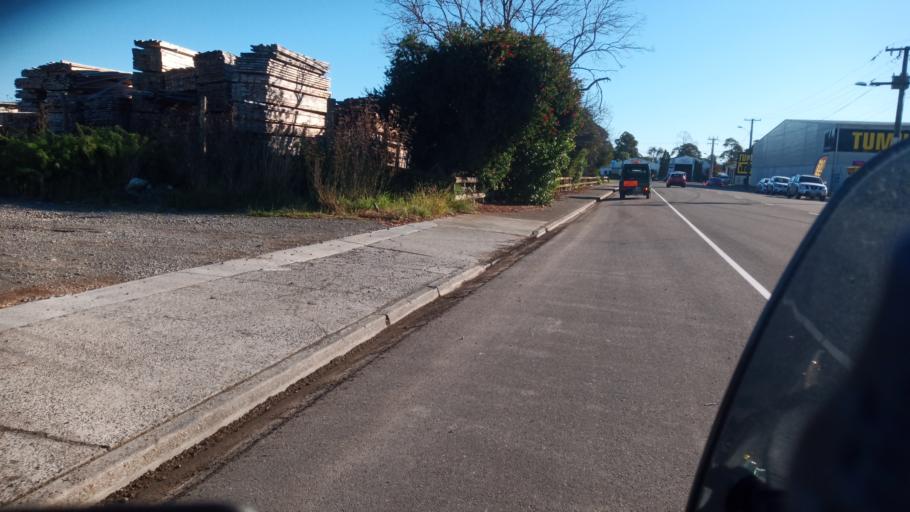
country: NZ
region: Hawke's Bay
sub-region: Napier City
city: Napier
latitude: -39.4917
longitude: 176.8842
